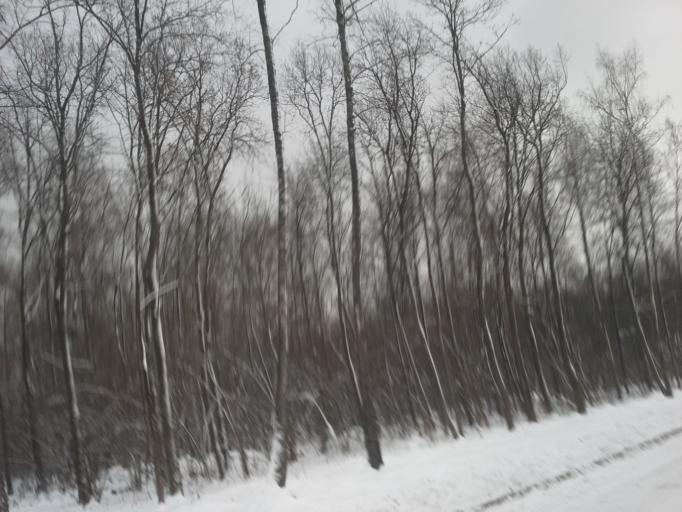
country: RU
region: Moskovskaya
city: Kommunarka
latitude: 55.5727
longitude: 37.5200
